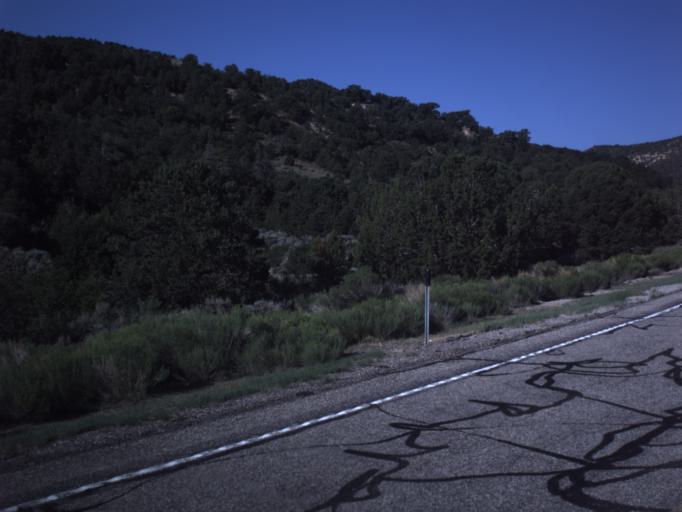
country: US
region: Utah
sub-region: Wayne County
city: Loa
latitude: 38.6726
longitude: -111.4101
